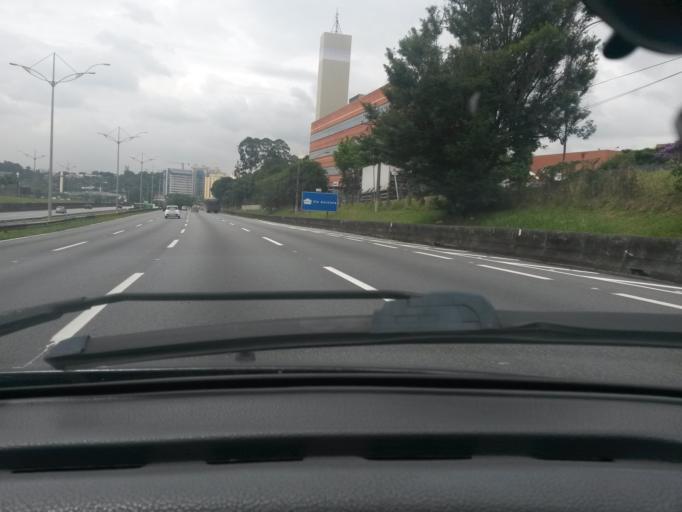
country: BR
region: Sao Paulo
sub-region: Sao Caetano Do Sul
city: Sao Caetano do Sul
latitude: -23.6326
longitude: -46.5965
